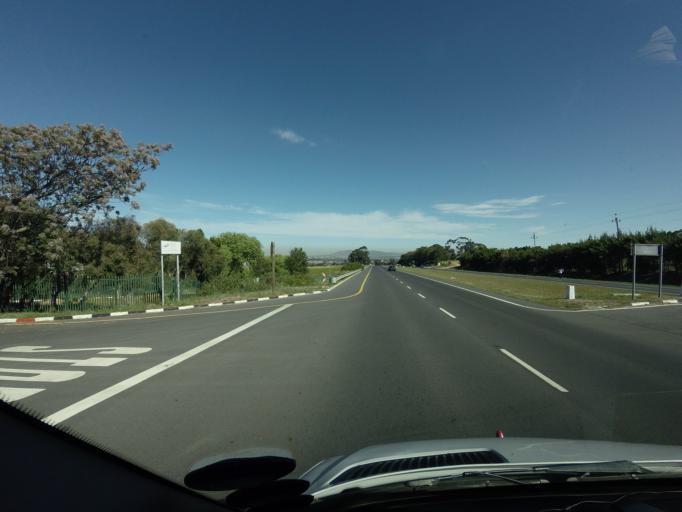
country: ZA
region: Western Cape
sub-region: City of Cape Town
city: Kraaifontein
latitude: -33.9576
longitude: 18.7230
